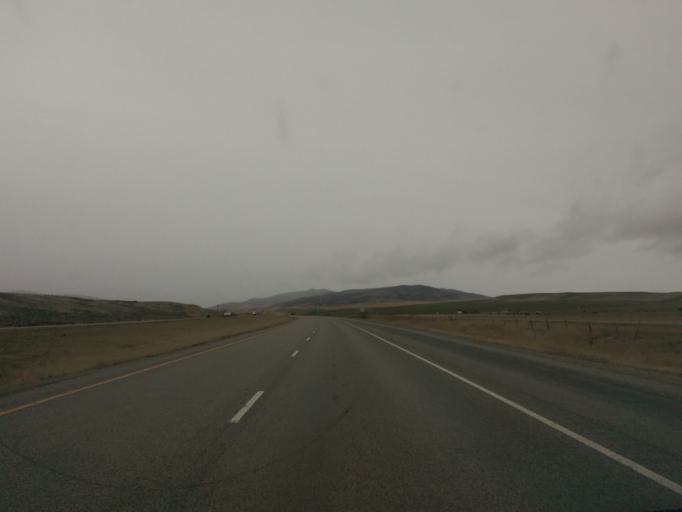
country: US
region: Montana
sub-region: Gallatin County
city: Three Forks
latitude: 45.9148
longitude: -111.7540
